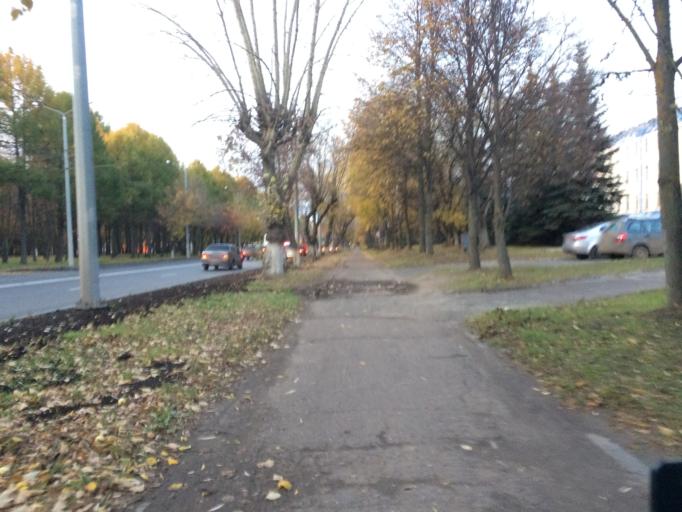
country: RU
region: Mariy-El
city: Yoshkar-Ola
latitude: 56.6114
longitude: 47.8804
